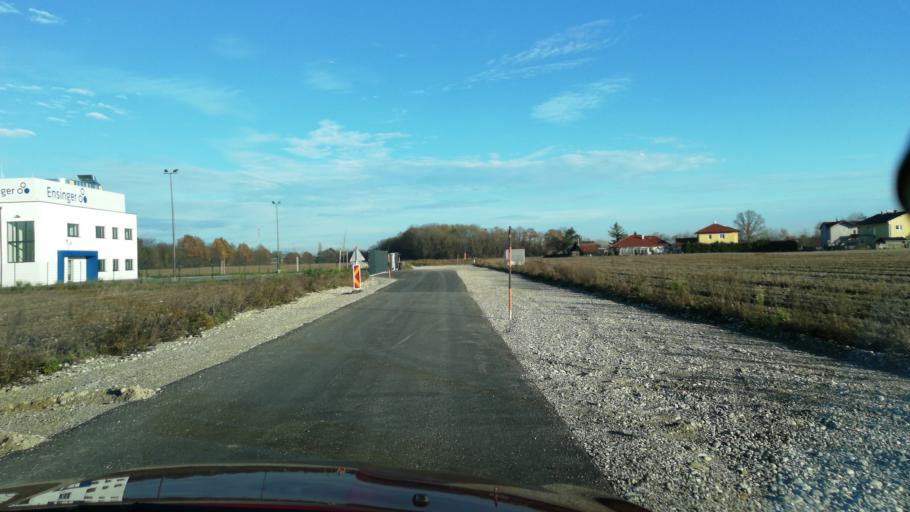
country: AT
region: Upper Austria
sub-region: Wels Stadt
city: Wels
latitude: 48.1895
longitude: 14.0400
